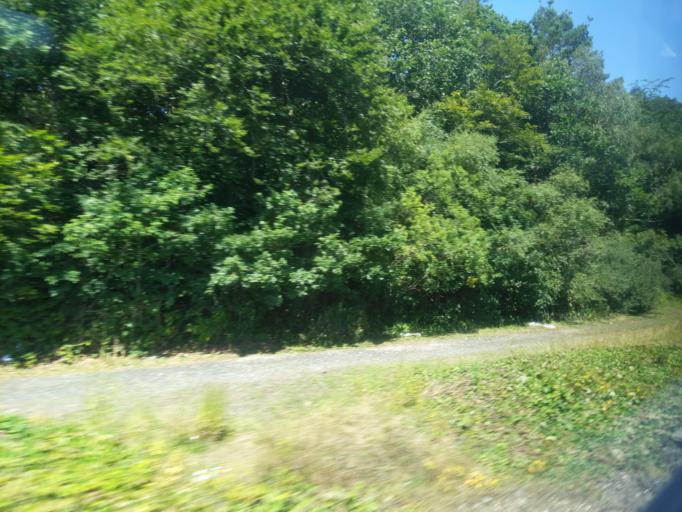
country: GB
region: England
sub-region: Devon
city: Ivybridge
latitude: 50.4081
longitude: -3.9665
